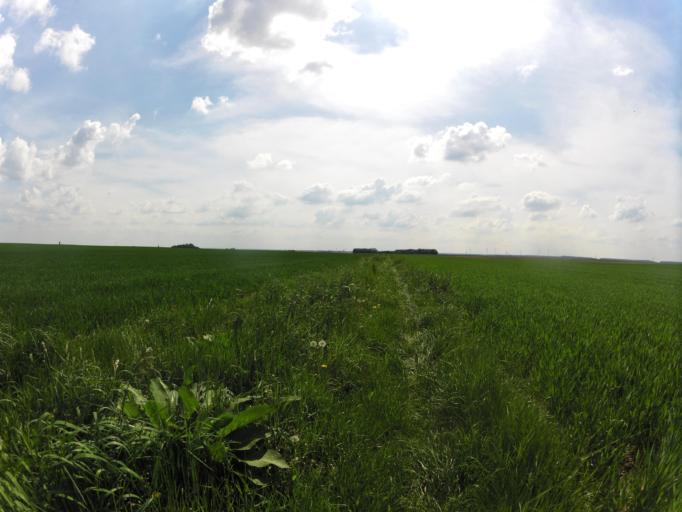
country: DE
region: Bavaria
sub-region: Regierungsbezirk Unterfranken
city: Giebelstadt
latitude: 49.6401
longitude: 9.9284
